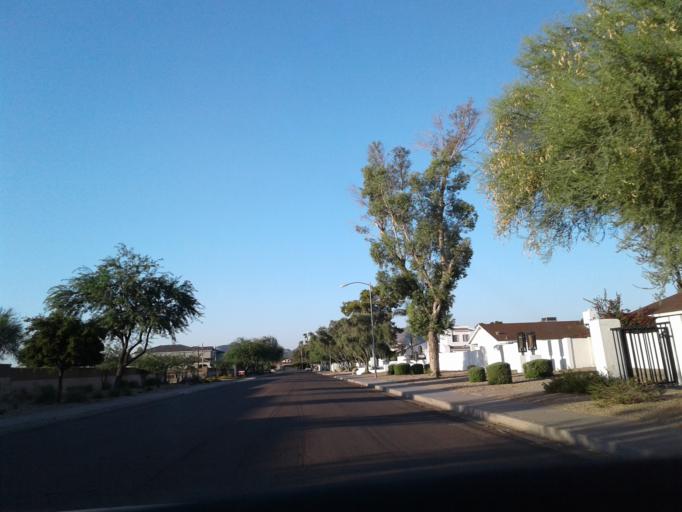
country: US
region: Arizona
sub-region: Maricopa County
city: Glendale
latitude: 33.6343
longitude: -112.0785
